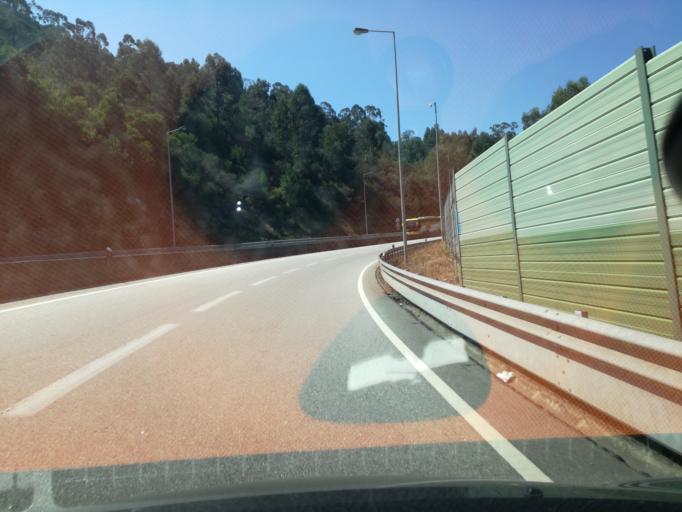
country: PT
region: Viana do Castelo
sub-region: Vila Nova de Cerveira
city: Vila Nova de Cerveira
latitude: 41.9152
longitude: -8.7781
